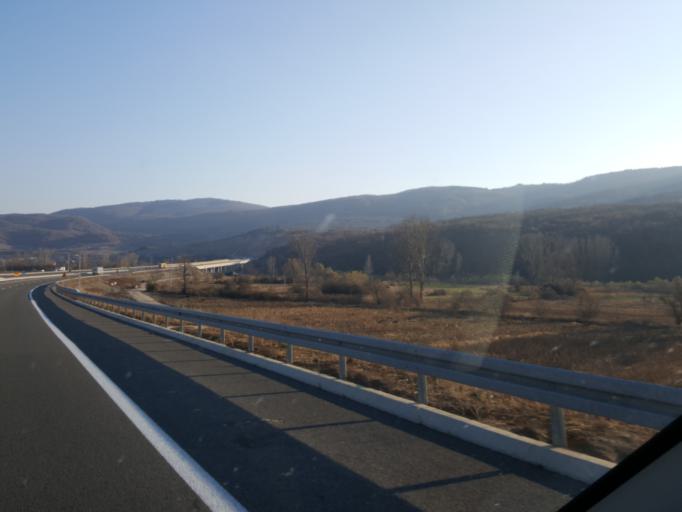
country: RS
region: Central Serbia
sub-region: Pirotski Okrug
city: Dimitrovgrad
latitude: 43.0166
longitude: 22.8002
